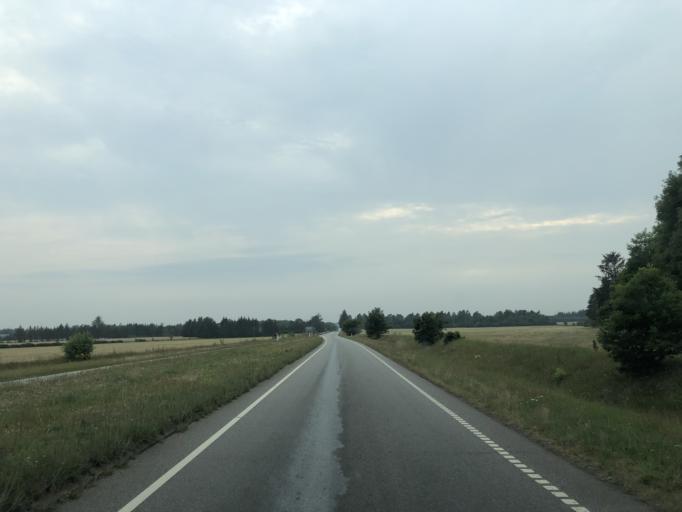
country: DK
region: Central Jutland
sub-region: Herning Kommune
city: Avlum
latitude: 56.3031
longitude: 8.8832
